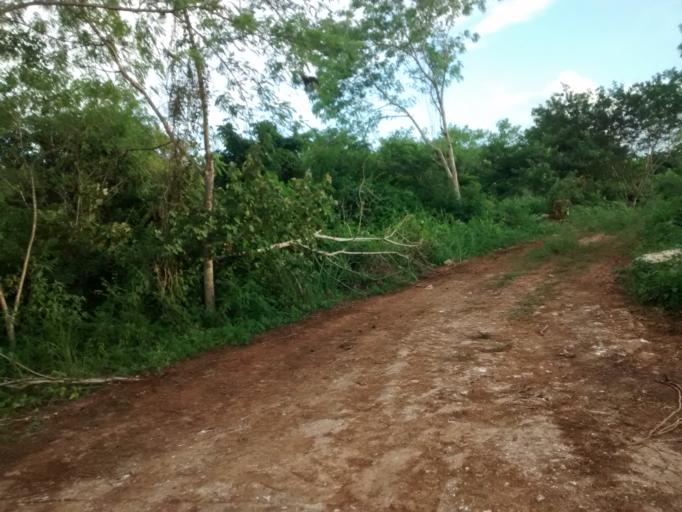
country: MX
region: Yucatan
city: Valladolid
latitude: 20.6867
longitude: -88.1792
